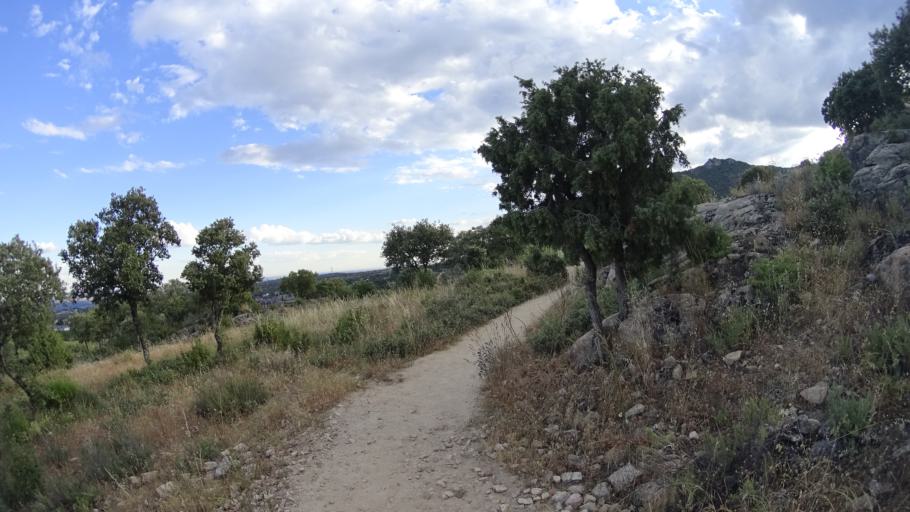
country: ES
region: Madrid
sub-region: Provincia de Madrid
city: Hoyo de Manzanares
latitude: 40.6296
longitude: -3.9118
